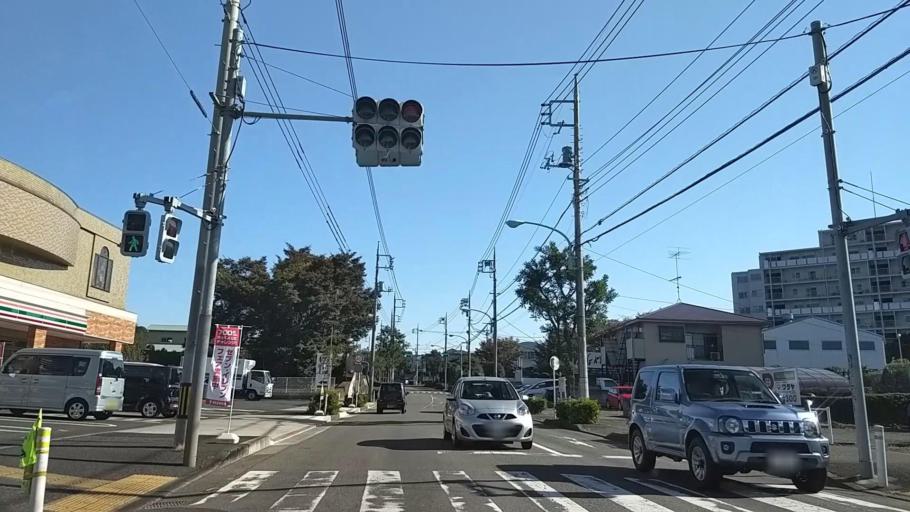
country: JP
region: Tokyo
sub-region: Machida-shi
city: Machida
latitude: 35.5192
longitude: 139.4654
